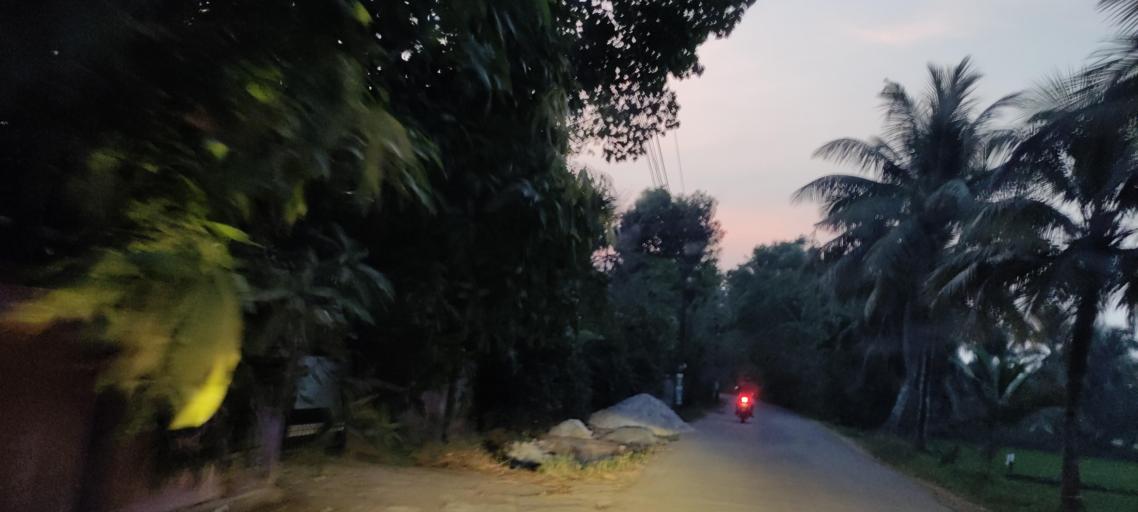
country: IN
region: Kerala
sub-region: Alappuzha
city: Mavelikara
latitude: 9.3213
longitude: 76.4549
